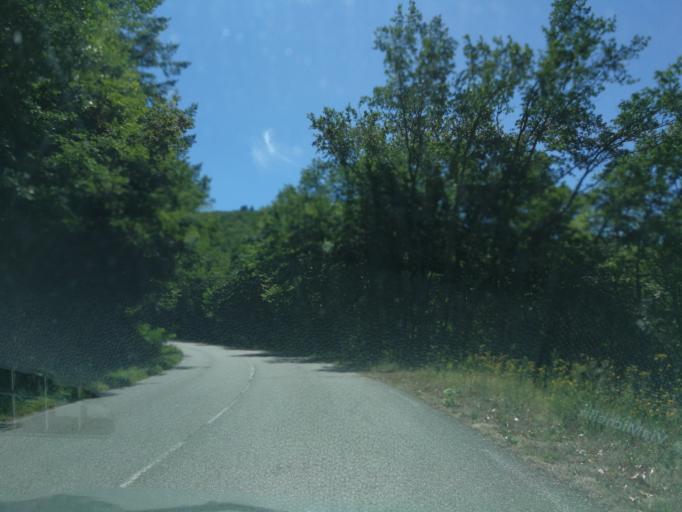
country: FR
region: Limousin
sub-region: Departement de la Correze
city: Argentat
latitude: 45.0732
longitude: 1.9453
